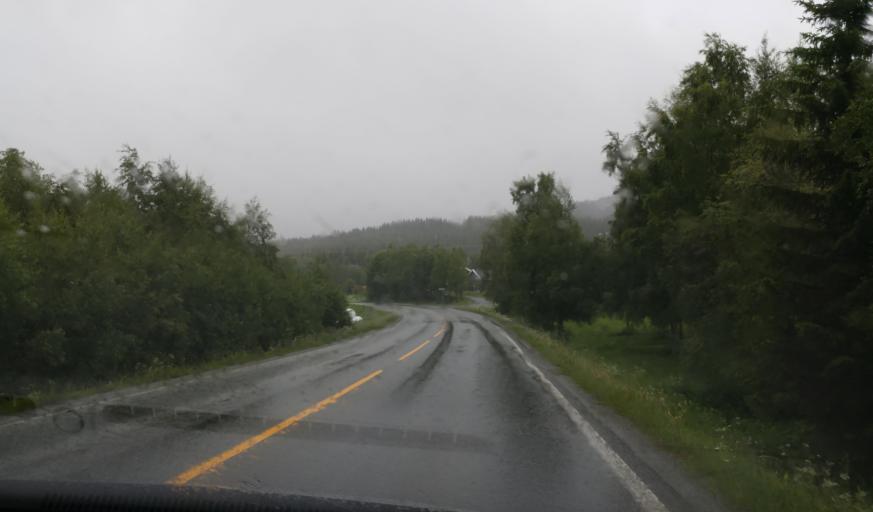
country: NO
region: Nord-Trondelag
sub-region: Stjordal
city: Stjordalshalsen
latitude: 63.4036
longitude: 10.9431
